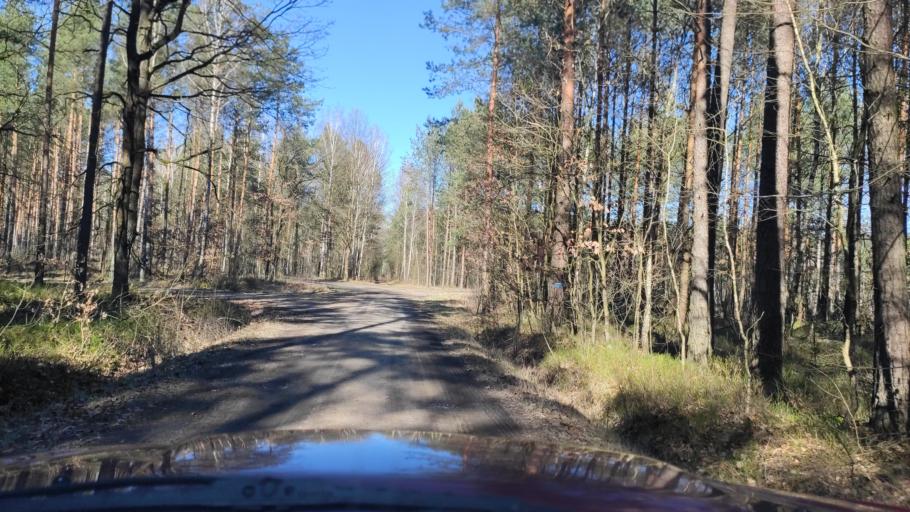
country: PL
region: Masovian Voivodeship
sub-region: Powiat kozienicki
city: Garbatka-Letnisko
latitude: 51.4401
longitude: 21.5424
